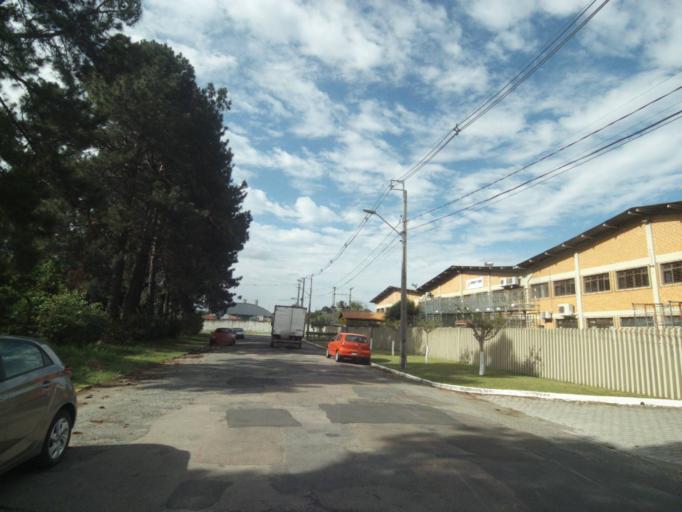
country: BR
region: Parana
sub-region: Curitiba
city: Curitiba
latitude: -25.4994
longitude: -49.3295
